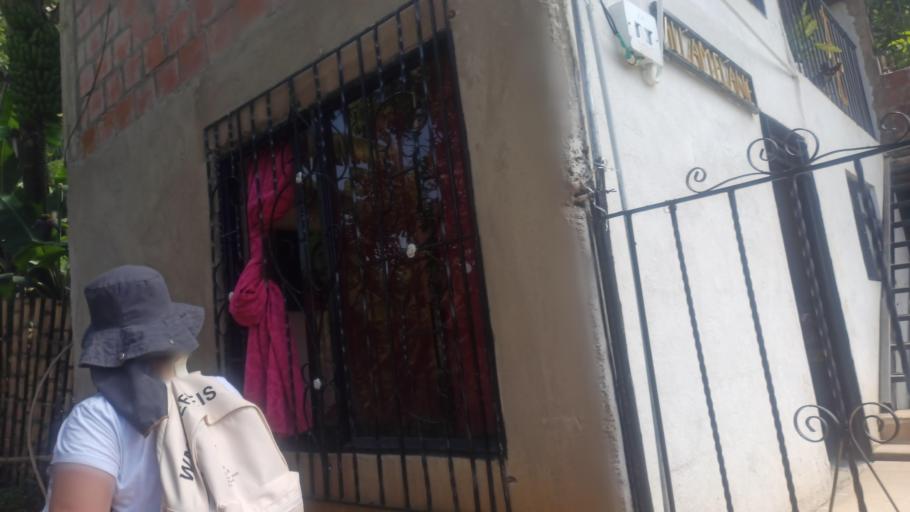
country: CO
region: Valle del Cauca
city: Jamundi
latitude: 3.1885
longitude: -76.6298
